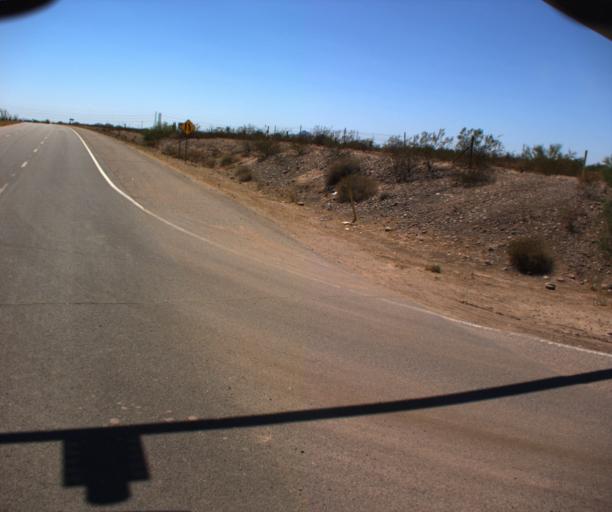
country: US
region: Arizona
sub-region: Maricopa County
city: Mesa
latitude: 33.5044
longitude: -111.7879
